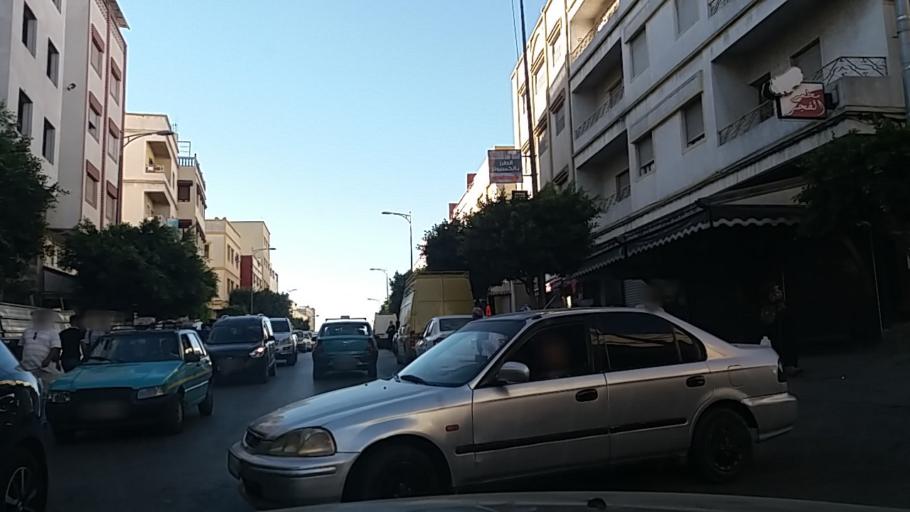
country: MA
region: Tanger-Tetouan
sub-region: Tanger-Assilah
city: Tangier
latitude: 35.7547
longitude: -5.8205
